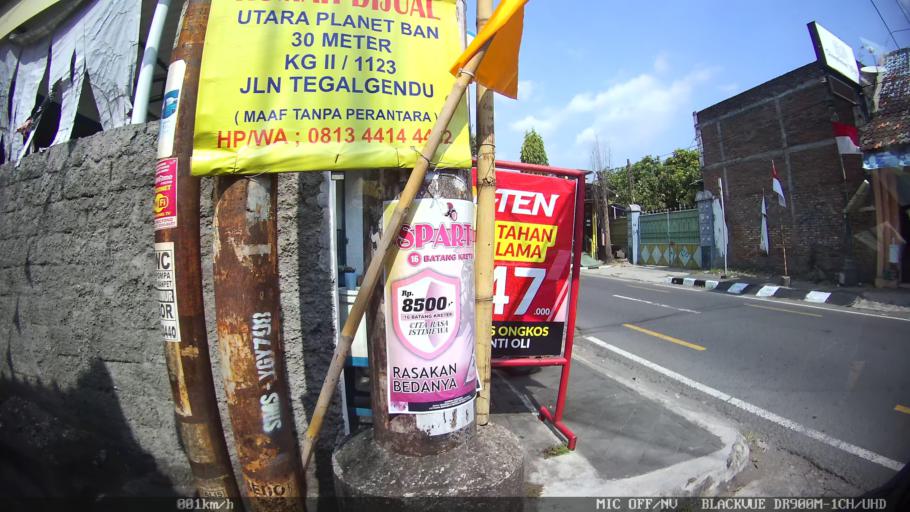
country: ID
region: Daerah Istimewa Yogyakarta
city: Yogyakarta
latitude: -7.8257
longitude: 110.3913
